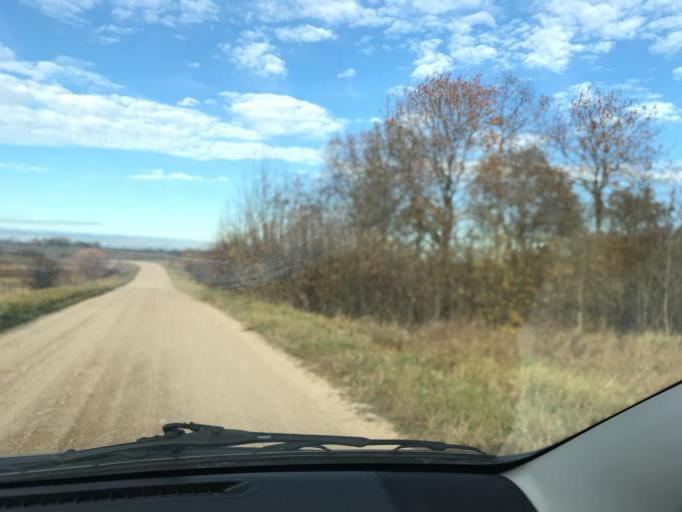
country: BY
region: Vitebsk
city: Haradok
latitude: 55.4532
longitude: 30.0357
